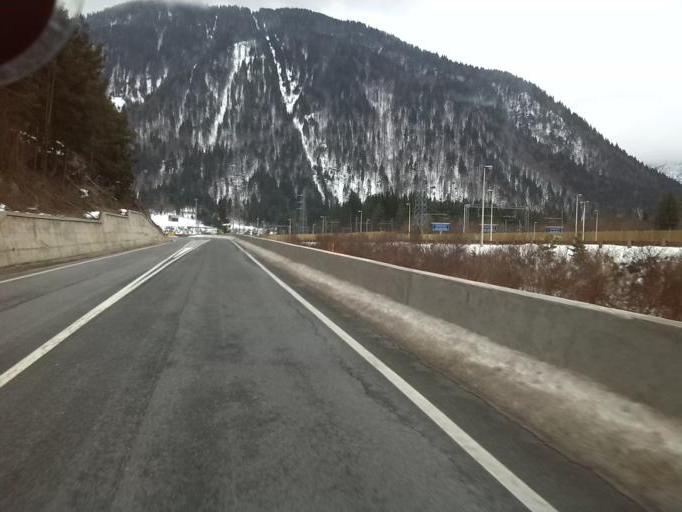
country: IT
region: Friuli Venezia Giulia
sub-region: Provincia di Udine
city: Malborghetto
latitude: 46.5030
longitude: 13.4964
